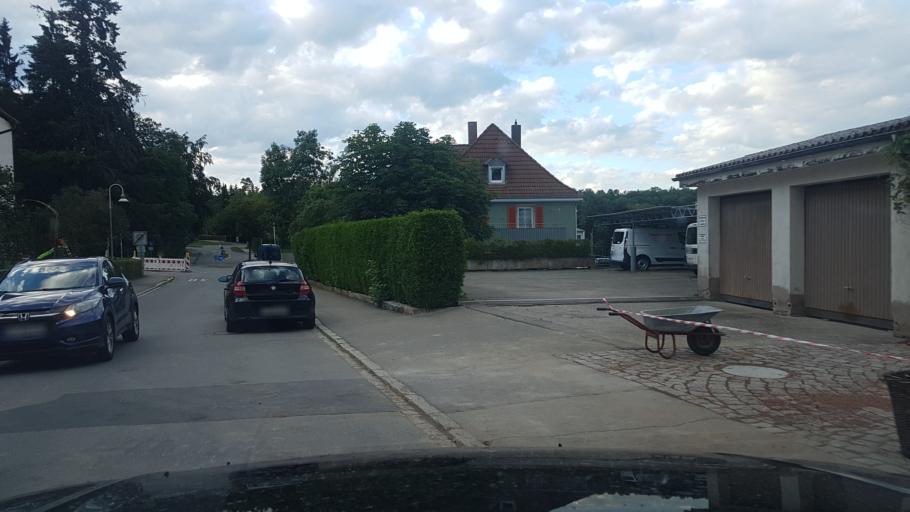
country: DE
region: Baden-Wuerttemberg
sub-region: Freiburg Region
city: Donaueschingen
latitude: 47.9561
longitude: 8.4842
